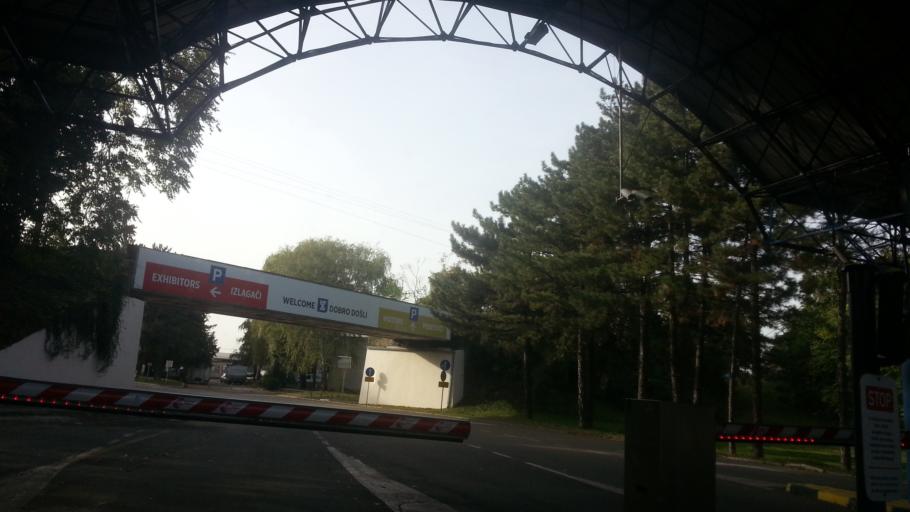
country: RS
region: Central Serbia
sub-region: Belgrade
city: Novi Beograd
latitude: 44.7987
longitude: 20.4417
